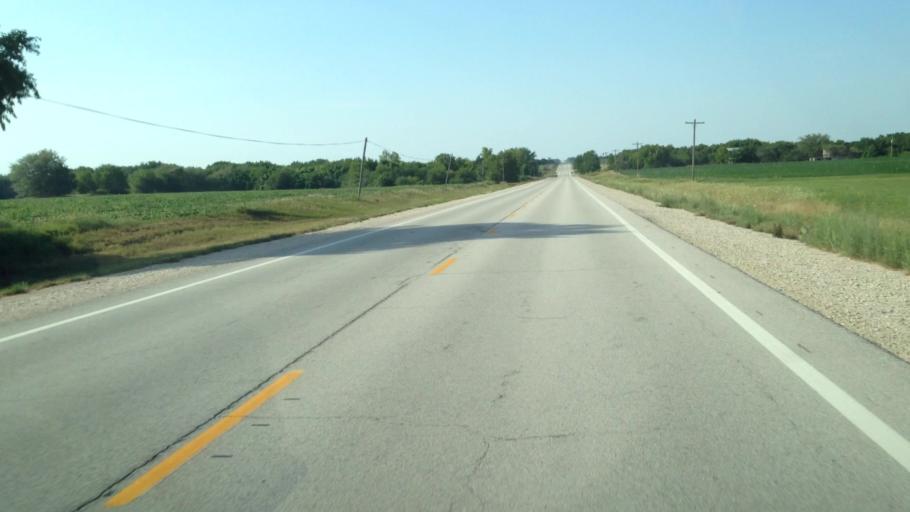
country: US
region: Kansas
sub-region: Anderson County
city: Garnett
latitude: 38.1033
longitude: -95.2429
